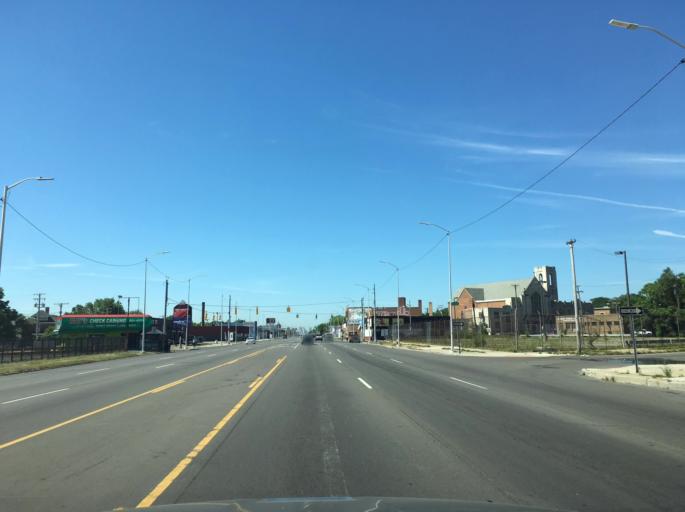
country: US
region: Michigan
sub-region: Macomb County
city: Eastpointe
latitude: 42.4280
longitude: -82.9824
